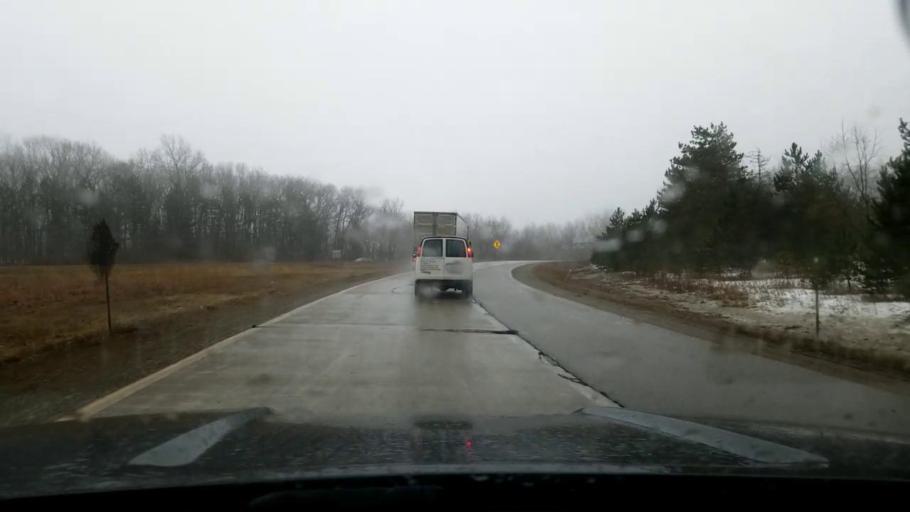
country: US
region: Michigan
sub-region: Jackson County
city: Jackson
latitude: 42.2760
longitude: -84.3598
